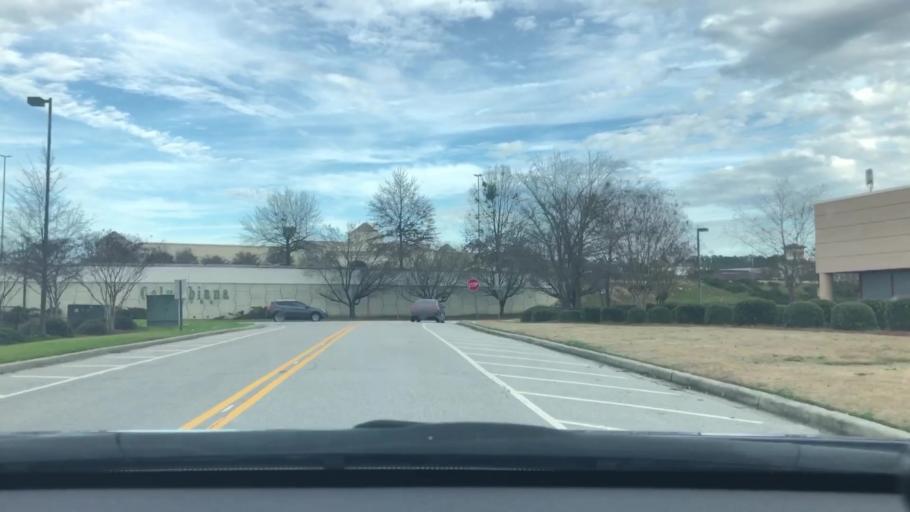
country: US
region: South Carolina
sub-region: Lexington County
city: Irmo
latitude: 34.0776
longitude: -81.1606
